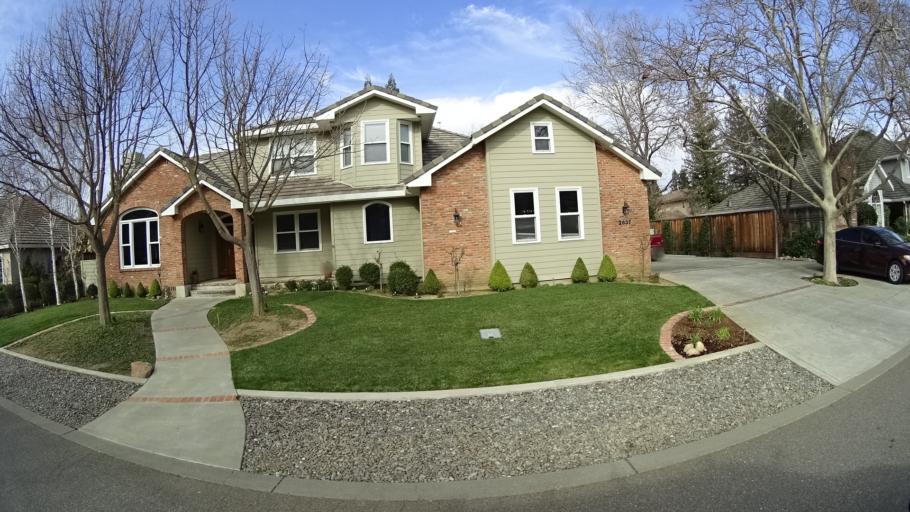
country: US
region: California
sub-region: Yolo County
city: Davis
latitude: 38.5385
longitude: -121.7193
